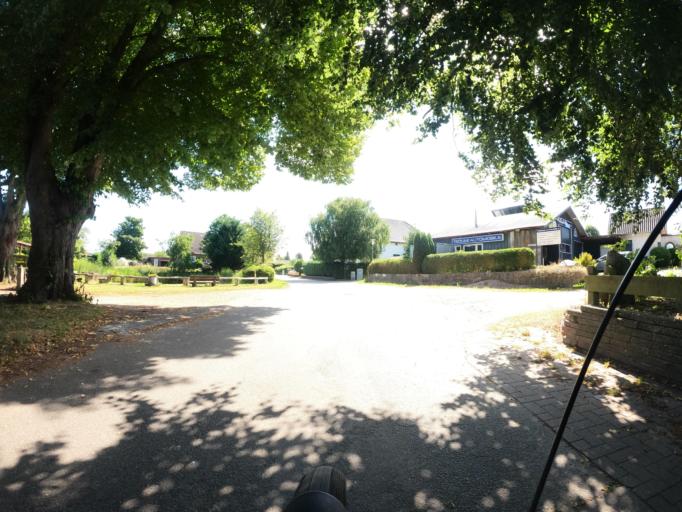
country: DE
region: Schleswig-Holstein
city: Dollerup
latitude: 54.7802
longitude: 9.6786
